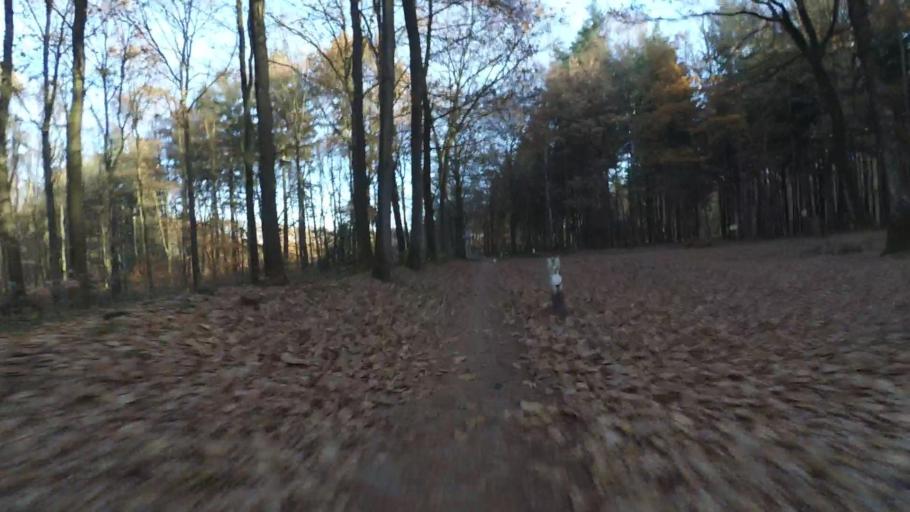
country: NL
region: Utrecht
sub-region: Gemeente Utrechtse Heuvelrug
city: Overberg
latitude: 52.0102
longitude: 5.5155
